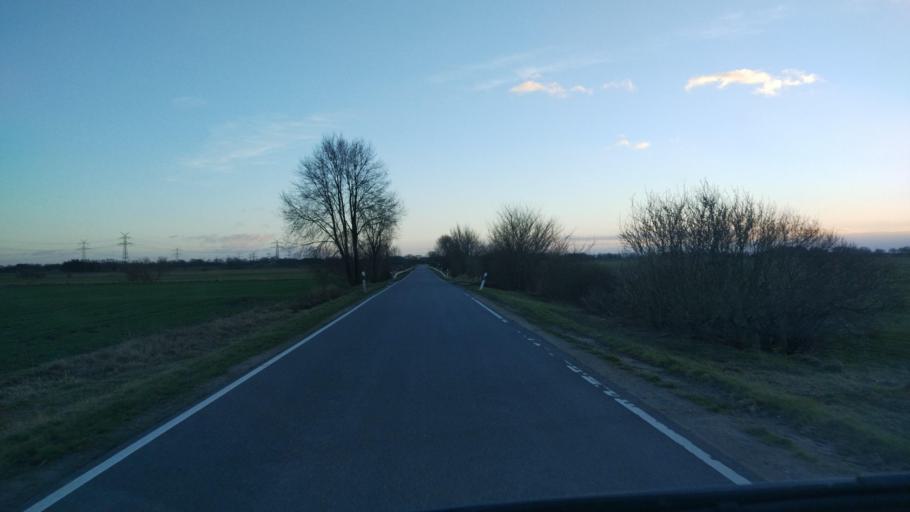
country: DE
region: Schleswig-Holstein
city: Gross Rheide
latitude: 54.4580
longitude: 9.4125
